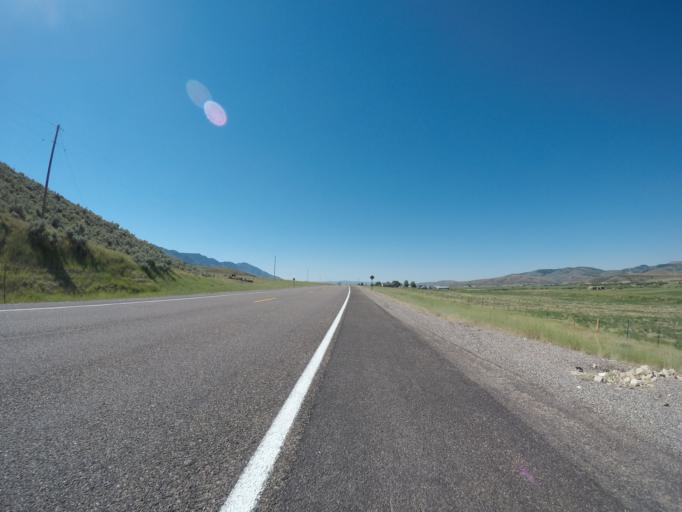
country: US
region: Idaho
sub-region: Bear Lake County
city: Montpelier
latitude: 42.3765
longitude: -111.0531
